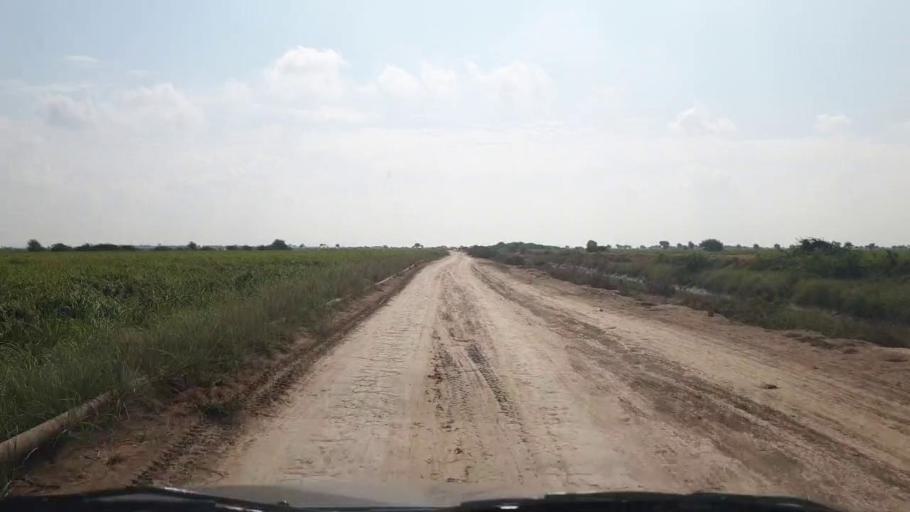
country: PK
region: Sindh
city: Kario
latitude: 24.5493
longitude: 68.5979
